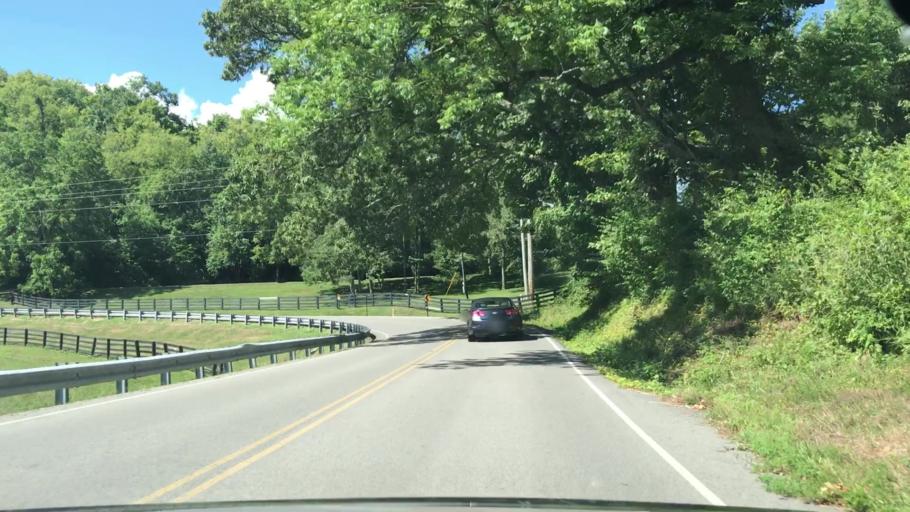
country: US
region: Tennessee
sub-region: Williamson County
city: Franklin
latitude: 35.9685
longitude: -86.8599
